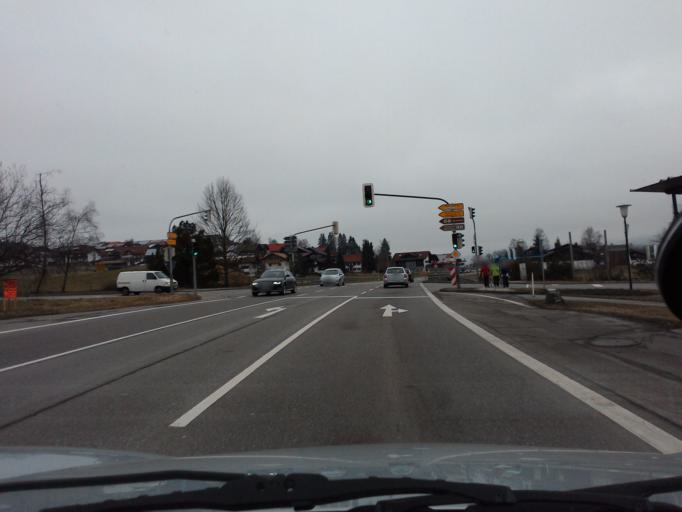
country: DE
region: Bavaria
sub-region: Swabia
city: Bolsterlang
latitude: 47.4599
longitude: 10.2672
